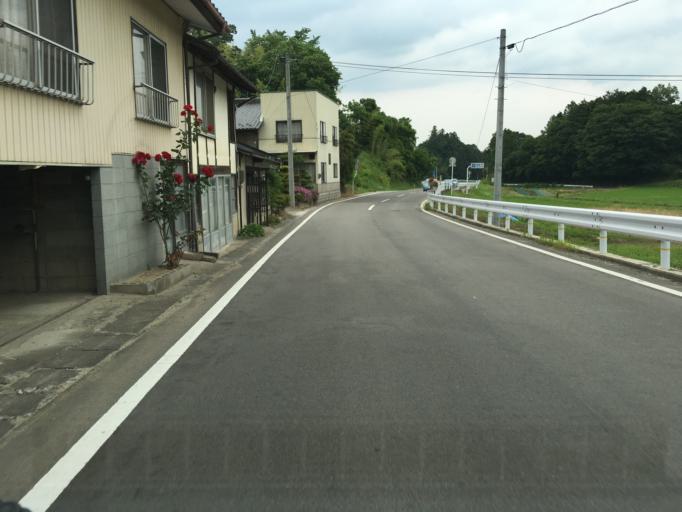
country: JP
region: Fukushima
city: Nihommatsu
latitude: 37.6391
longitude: 140.5359
